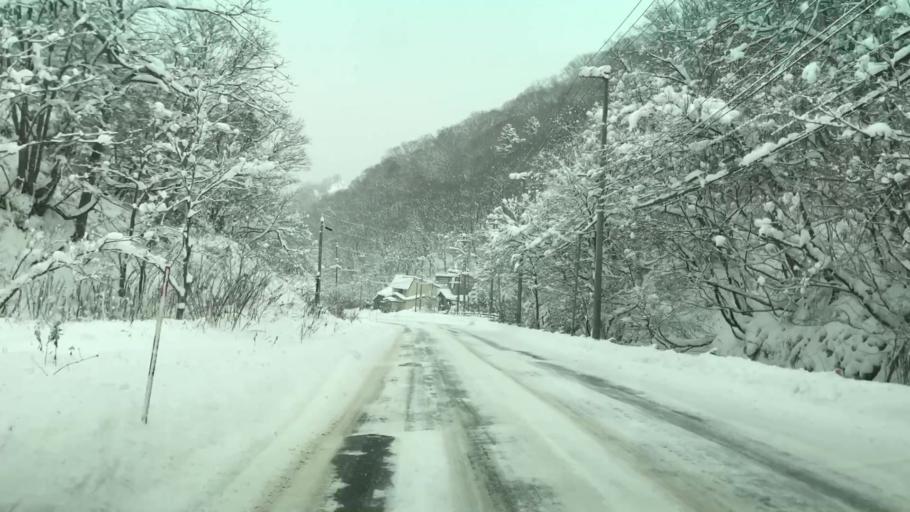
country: JP
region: Hokkaido
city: Yoichi
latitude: 43.2303
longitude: 140.7353
